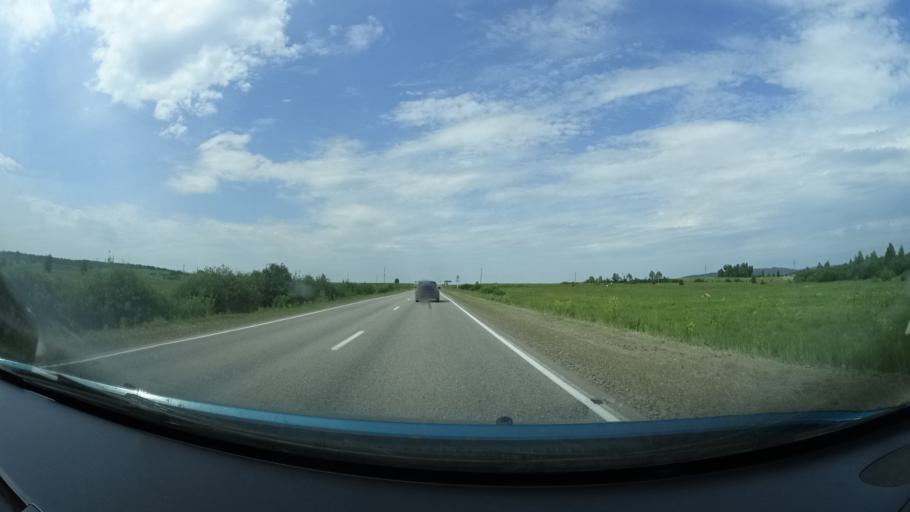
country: RU
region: Perm
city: Barda
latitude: 57.0295
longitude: 55.5510
